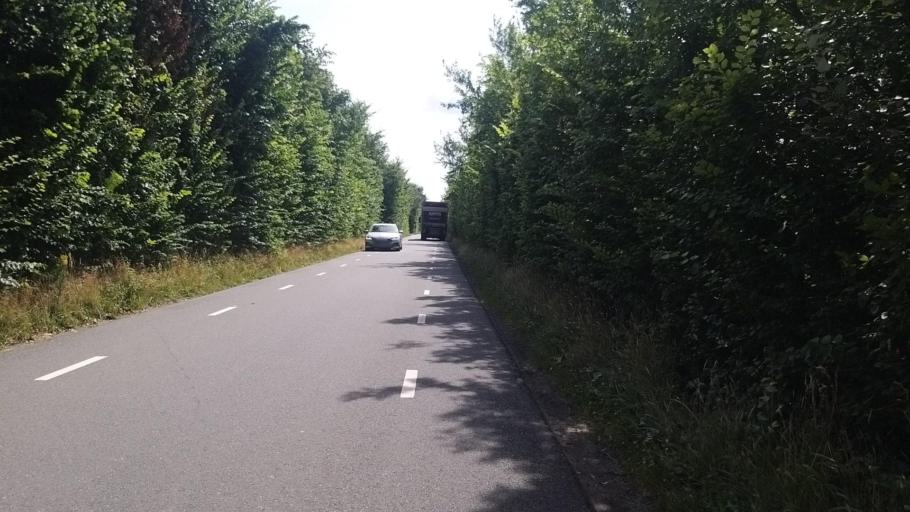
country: NL
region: North Holland
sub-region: Gemeente Texel
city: Den Burg
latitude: 53.0881
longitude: 4.7800
